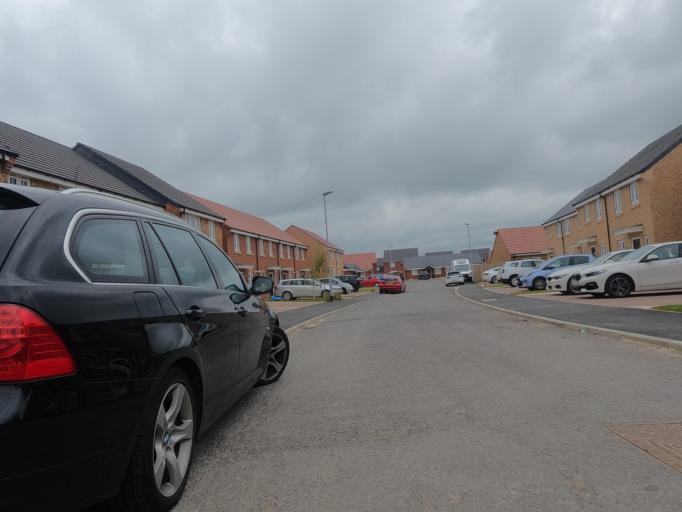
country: GB
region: England
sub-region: Northumberland
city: Blyth
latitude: 55.1053
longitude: -1.5343
